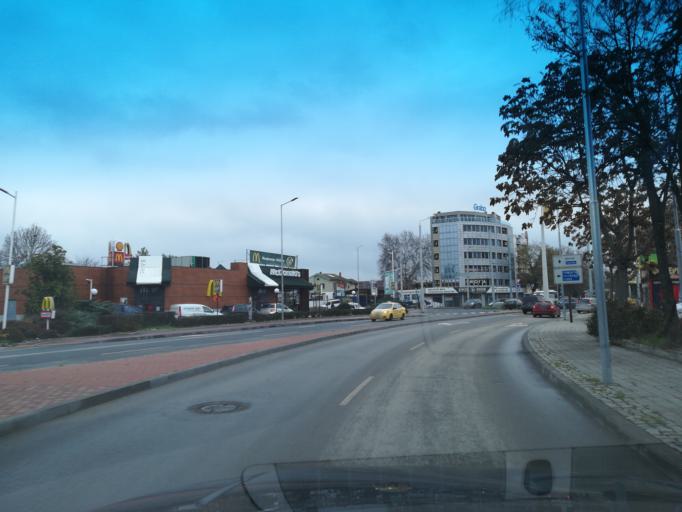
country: BG
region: Plovdiv
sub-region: Obshtina Plovdiv
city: Plovdiv
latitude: 42.1538
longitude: 24.7631
